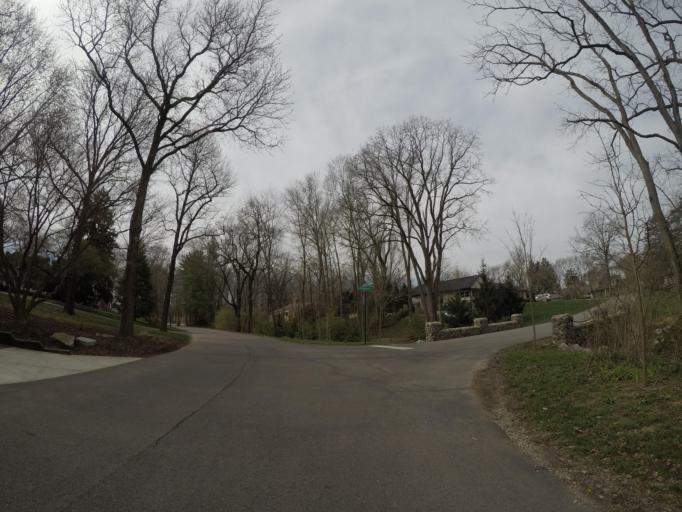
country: US
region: Ohio
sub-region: Franklin County
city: Upper Arlington
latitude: 40.0173
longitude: -83.0829
